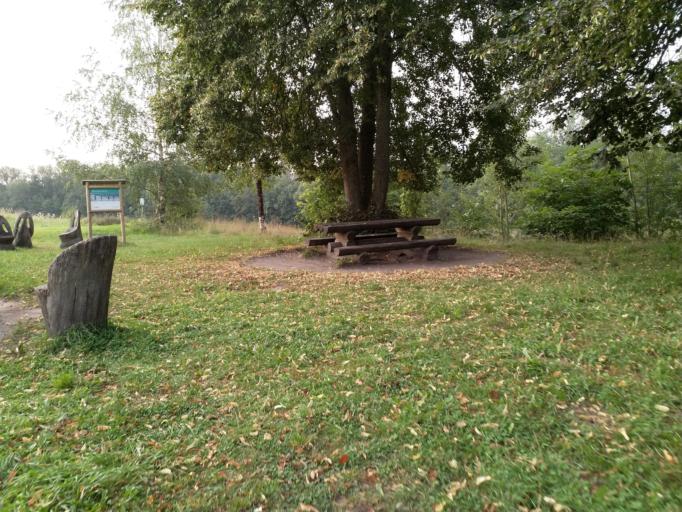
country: LV
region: Kuldigas Rajons
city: Kuldiga
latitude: 56.9681
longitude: 21.9820
